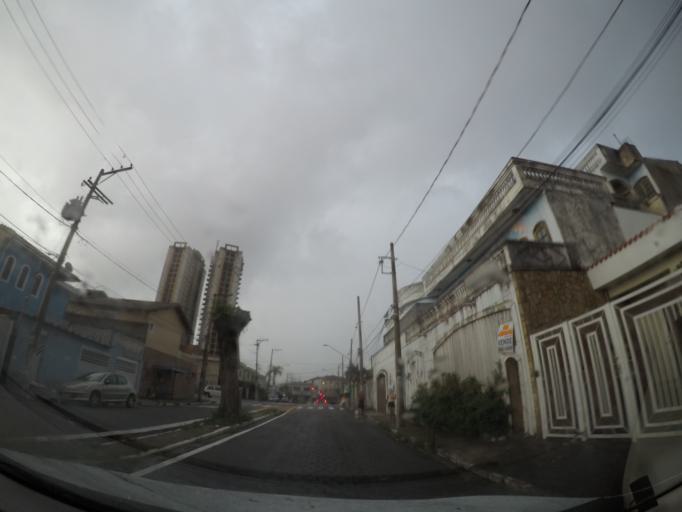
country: BR
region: Sao Paulo
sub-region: Guarulhos
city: Guarulhos
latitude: -23.4637
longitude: -46.5555
